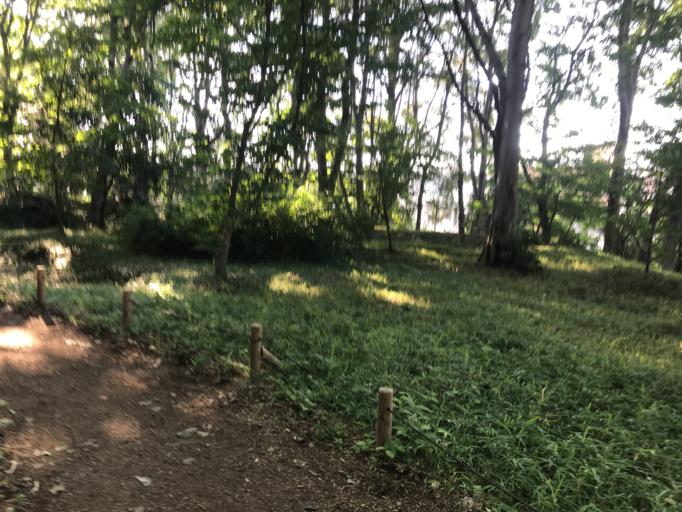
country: JP
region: Tokyo
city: Tokyo
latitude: 35.6266
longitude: 139.7066
